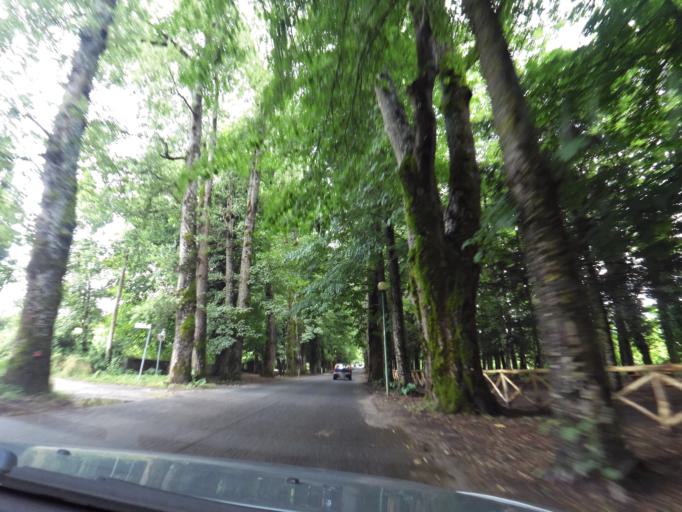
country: IT
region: Calabria
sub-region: Provincia di Vibo-Valentia
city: Serra San Bruno
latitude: 38.5695
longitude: 16.3231
